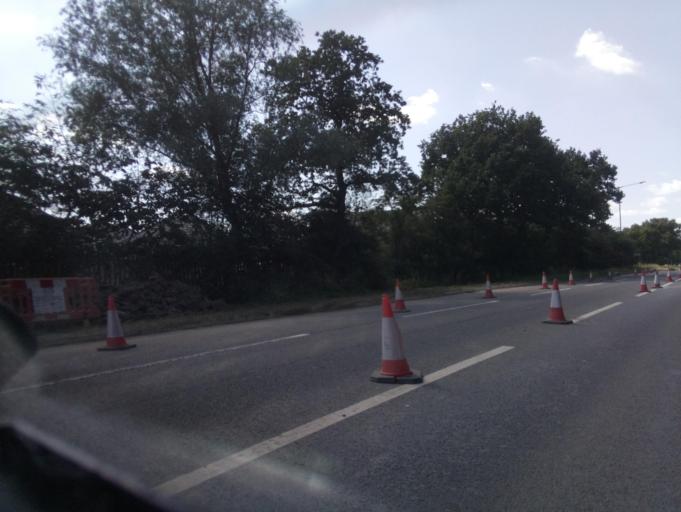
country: GB
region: England
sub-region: Leicestershire
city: Stoke Golding
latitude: 52.5395
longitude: -1.4269
